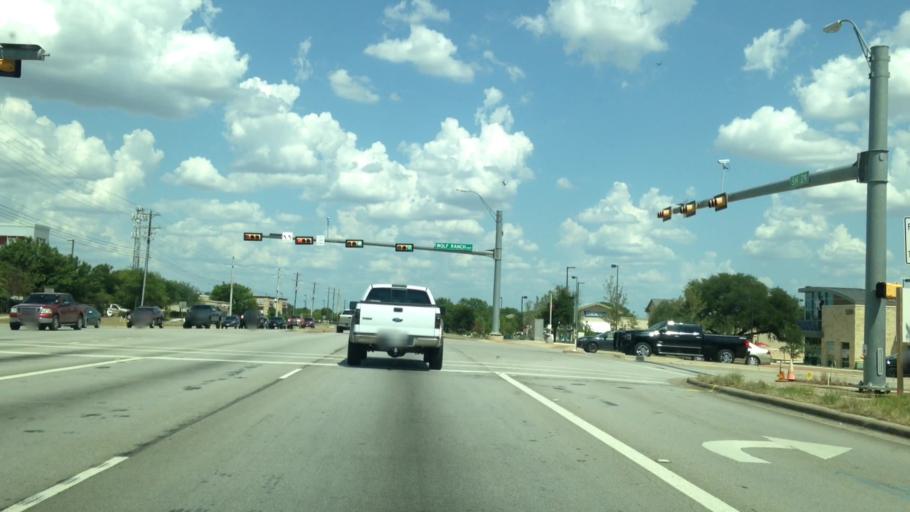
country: US
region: Texas
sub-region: Williamson County
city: Georgetown
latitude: 30.6329
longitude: -97.7008
